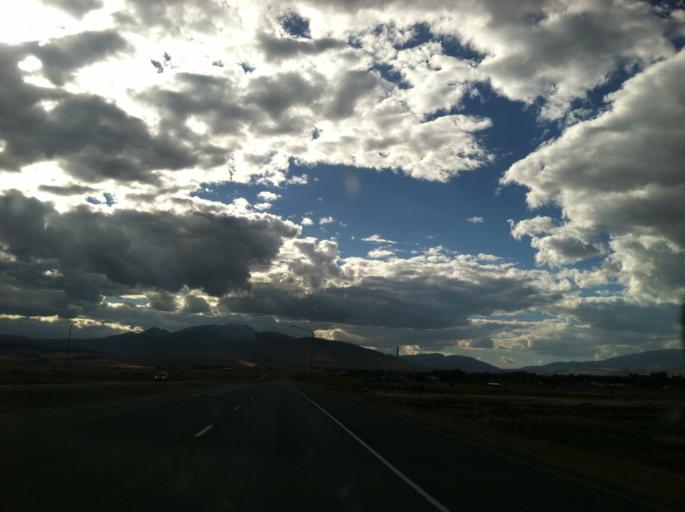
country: US
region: Montana
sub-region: Deer Lodge County
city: Warm Springs
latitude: 46.0957
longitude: -112.8085
